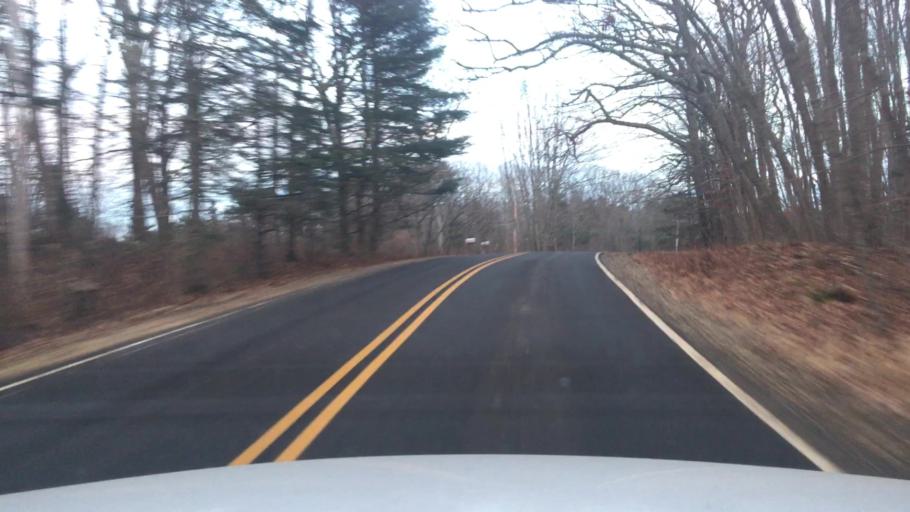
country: US
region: Maine
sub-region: Lincoln County
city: Bristol
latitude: 43.9182
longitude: -69.5310
